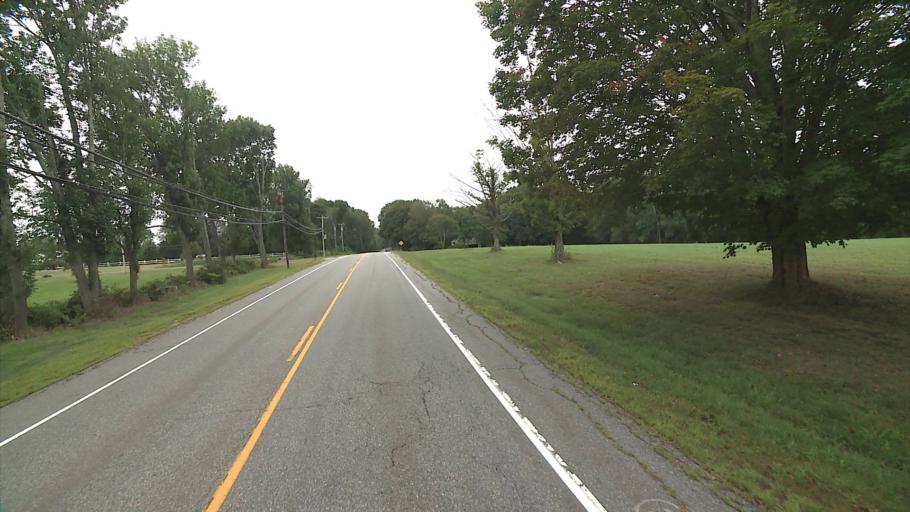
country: US
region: Connecticut
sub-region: Hartford County
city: Manchester
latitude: 41.7374
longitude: -72.4358
